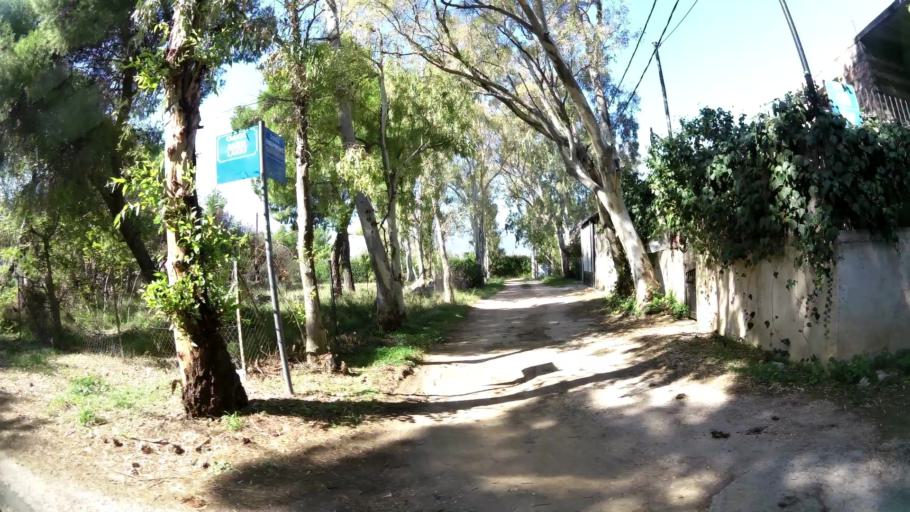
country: GR
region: Attica
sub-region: Nomarchia Athinas
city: Lykovrysi
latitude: 38.0875
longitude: 23.7776
